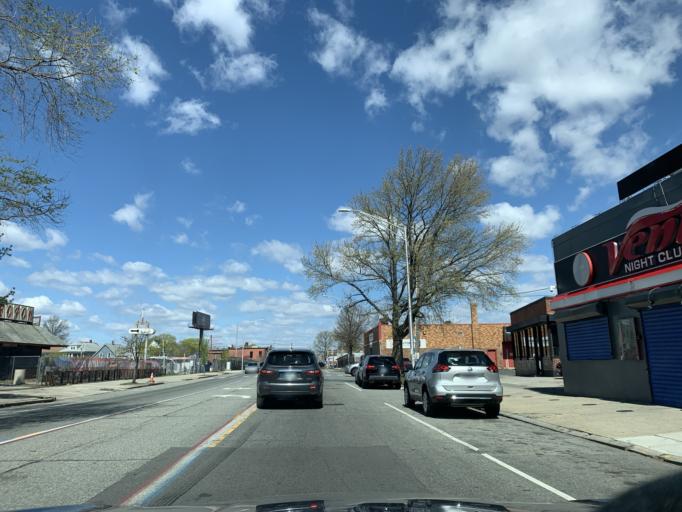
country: US
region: Rhode Island
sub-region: Providence County
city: Providence
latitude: 41.7933
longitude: -71.4085
